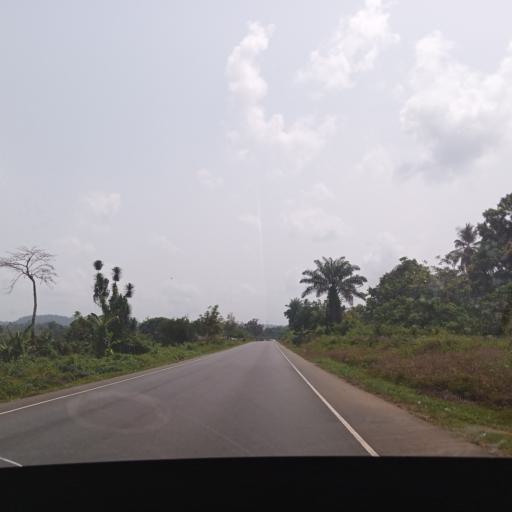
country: LR
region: Margibi
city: Kakata
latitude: 6.2338
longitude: -10.2817
